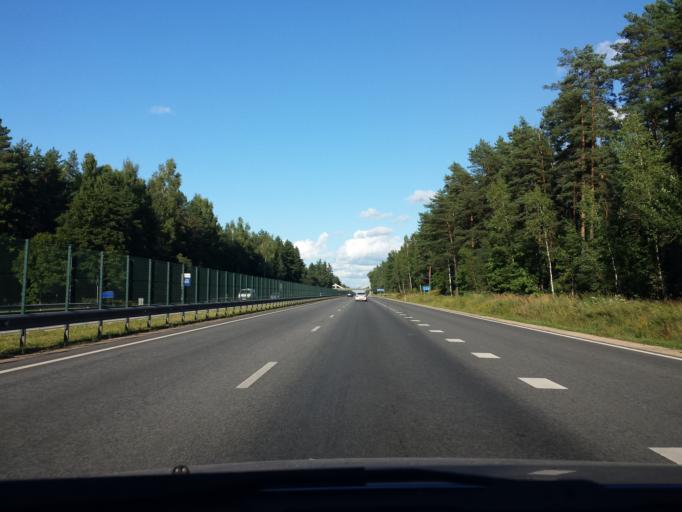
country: LV
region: Riga
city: Bergi
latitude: 57.0069
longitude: 24.2986
